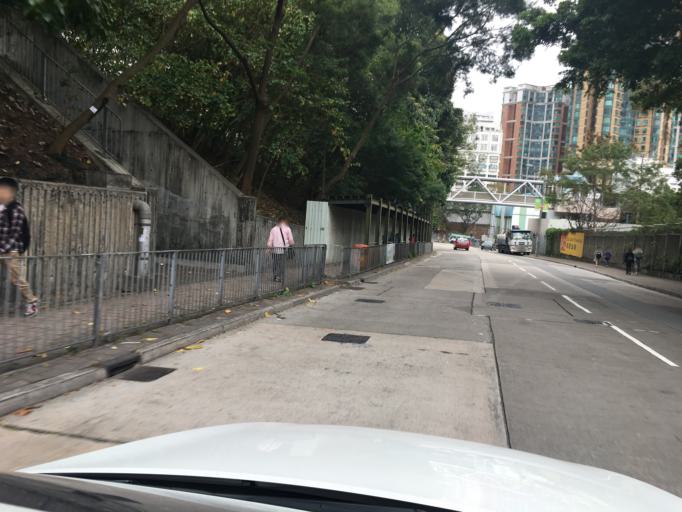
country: HK
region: Kowloon City
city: Kowloon
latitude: 22.3182
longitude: 114.1805
